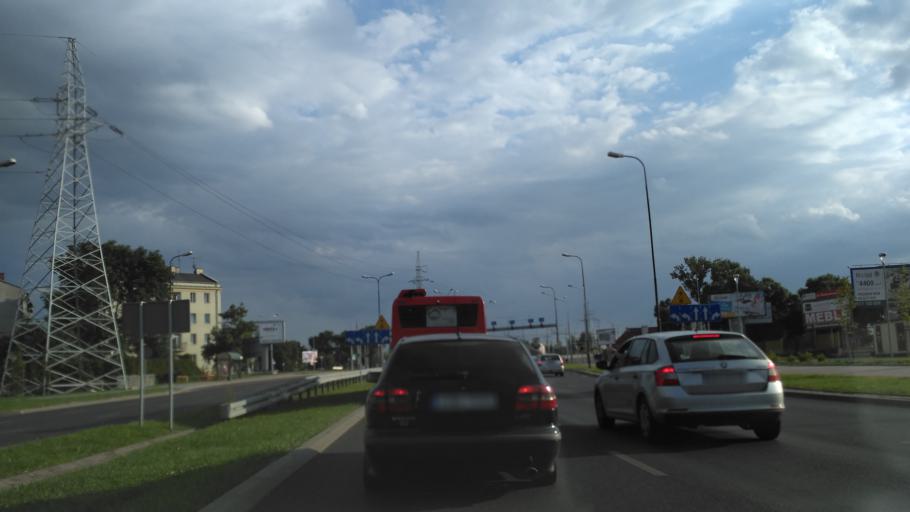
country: PL
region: Lublin Voivodeship
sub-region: Powiat lubelski
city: Lublin
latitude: 51.2363
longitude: 22.5694
